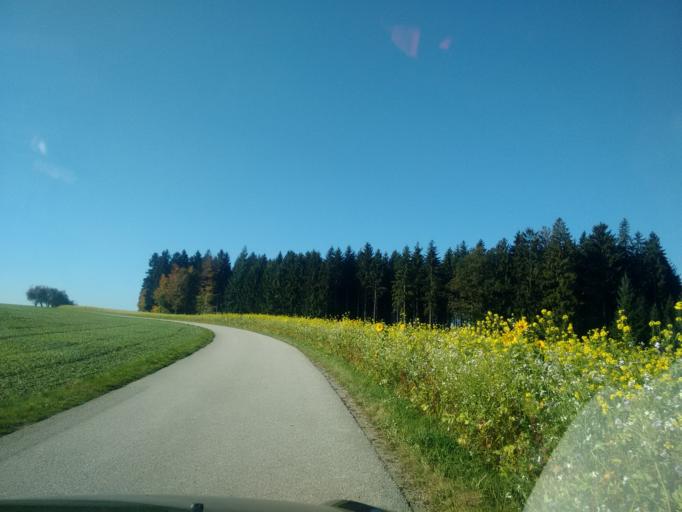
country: AT
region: Upper Austria
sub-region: Politischer Bezirk Rohrbach
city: Atzesberg
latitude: 48.4269
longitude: 13.8997
